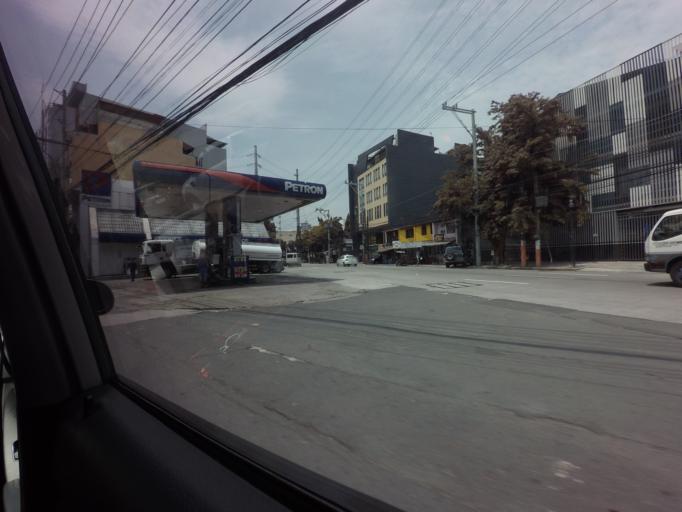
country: PH
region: Metro Manila
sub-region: City of Manila
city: Quiapo
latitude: 14.5805
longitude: 120.9886
